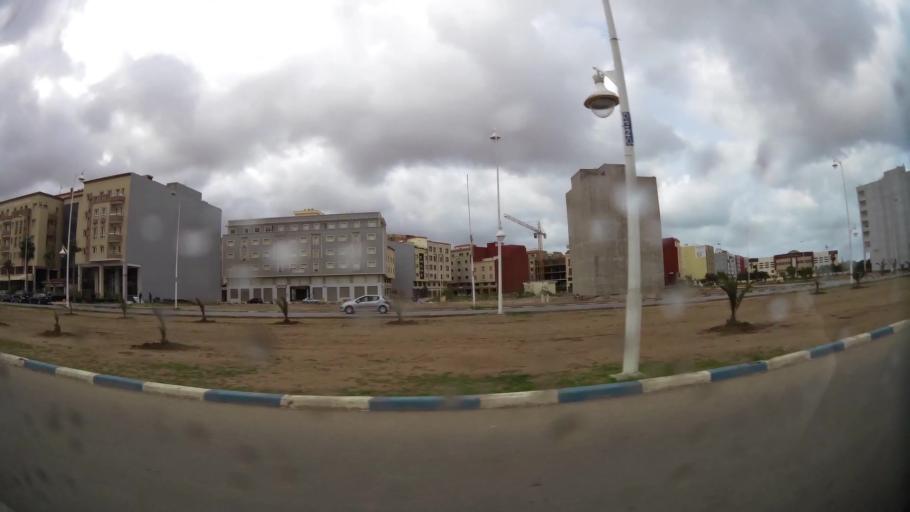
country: MA
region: Oriental
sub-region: Nador
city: Nador
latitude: 35.1521
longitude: -2.9249
